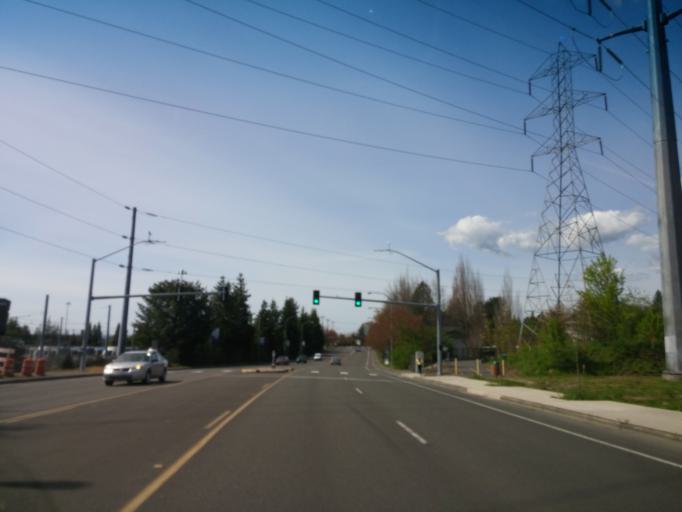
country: US
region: Oregon
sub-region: Washington County
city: Aloha
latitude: 45.5096
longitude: -122.8459
